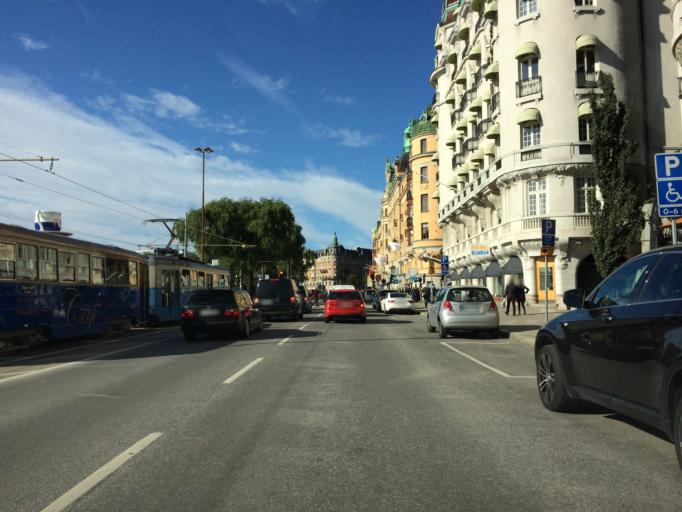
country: SE
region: Stockholm
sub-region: Stockholms Kommun
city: OEstermalm
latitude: 59.3318
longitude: 18.0806
